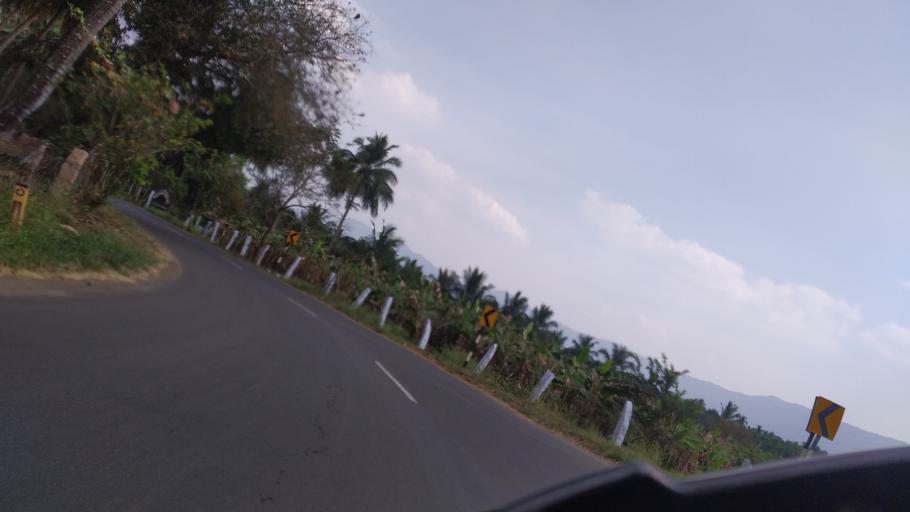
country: IN
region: Tamil Nadu
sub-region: Coimbatore
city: Perur
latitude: 10.9591
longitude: 76.7497
